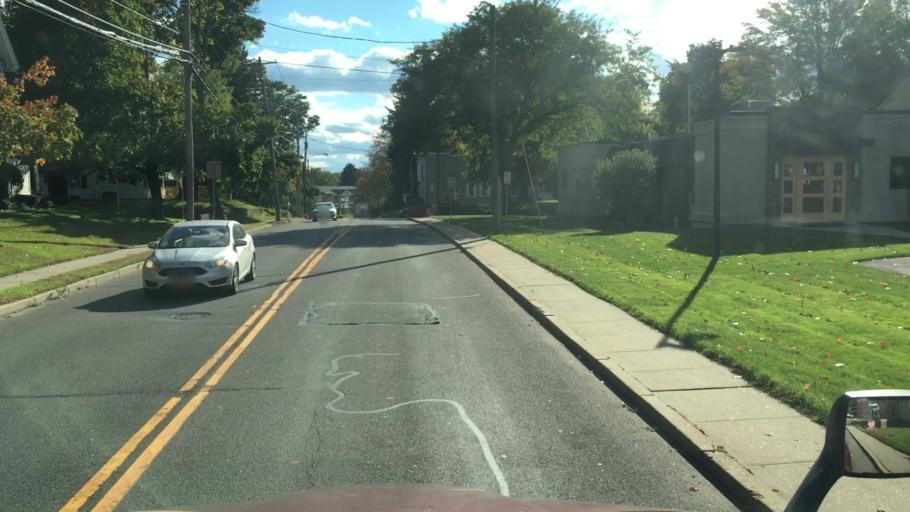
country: US
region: New York
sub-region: Schenectady County
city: Scotia
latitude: 42.8283
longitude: -73.9604
